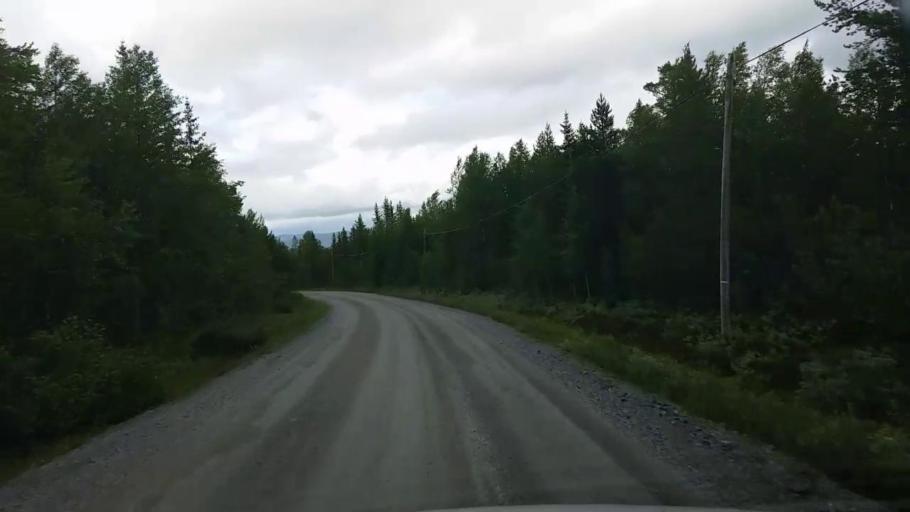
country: NO
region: Hedmark
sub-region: Engerdal
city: Engerdal
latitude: 62.4083
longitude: 12.6705
